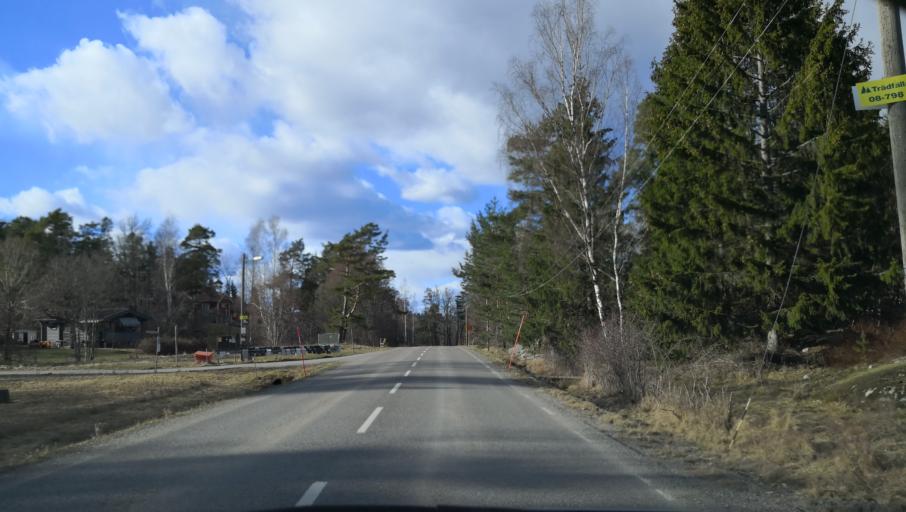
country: SE
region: Stockholm
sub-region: Varmdo Kommun
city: Hemmesta
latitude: 59.2832
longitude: 18.4939
